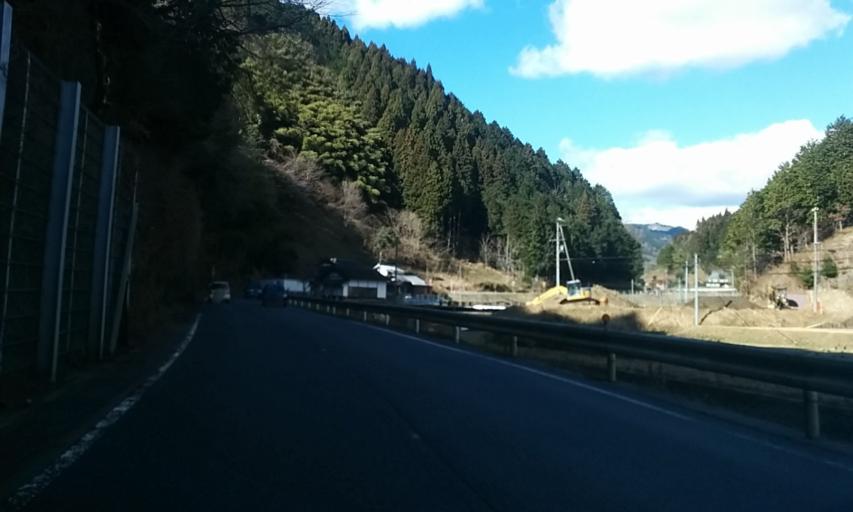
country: JP
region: Kyoto
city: Fukuchiyama
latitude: 35.3521
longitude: 135.0582
